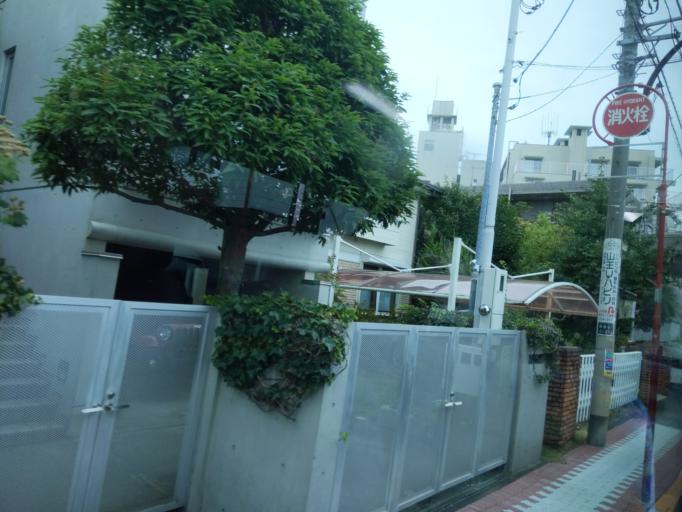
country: JP
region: Kanagawa
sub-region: Kawasaki-shi
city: Kawasaki
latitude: 35.5924
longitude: 139.6932
